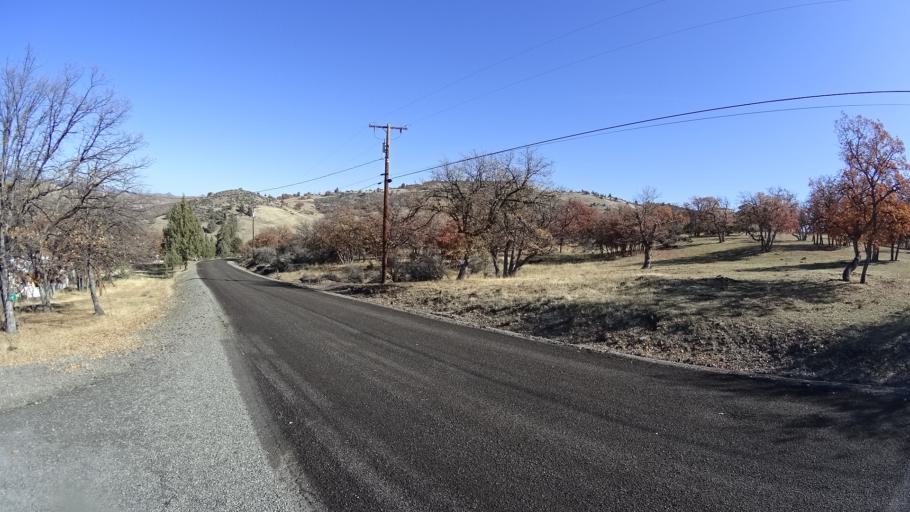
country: US
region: California
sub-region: Siskiyou County
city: Montague
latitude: 41.8851
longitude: -122.4840
